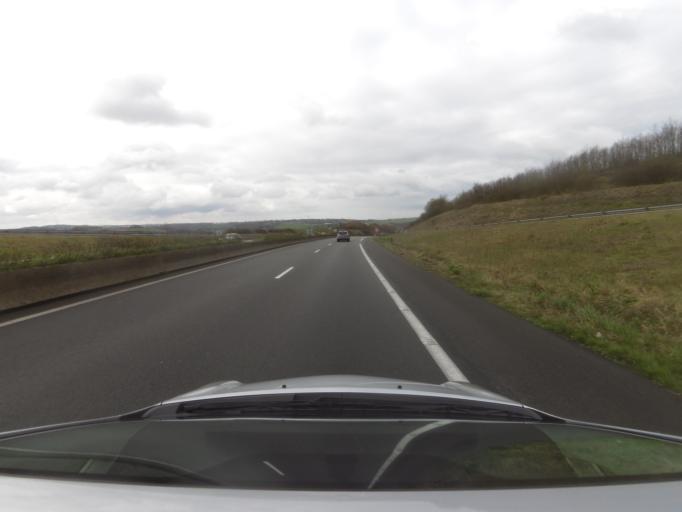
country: FR
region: Nord-Pas-de-Calais
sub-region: Departement du Pas-de-Calais
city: Wimille
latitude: 50.7701
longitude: 1.6480
